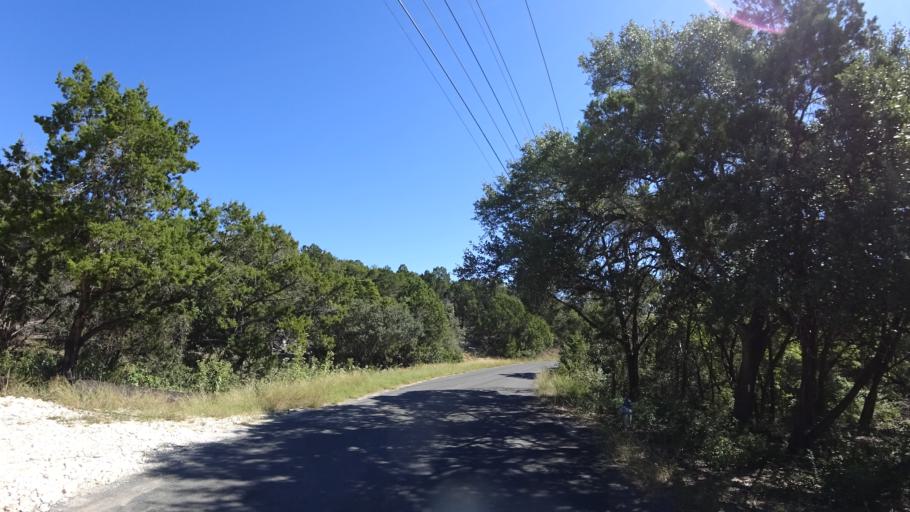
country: US
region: Texas
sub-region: Travis County
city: West Lake Hills
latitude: 30.3070
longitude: -97.8131
